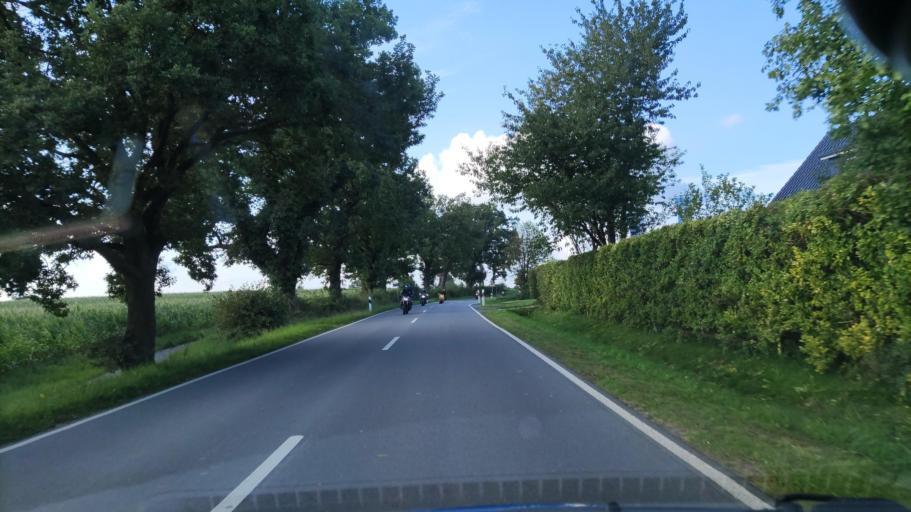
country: DE
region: Schleswig-Holstein
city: Glasau
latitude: 54.0466
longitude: 10.5309
